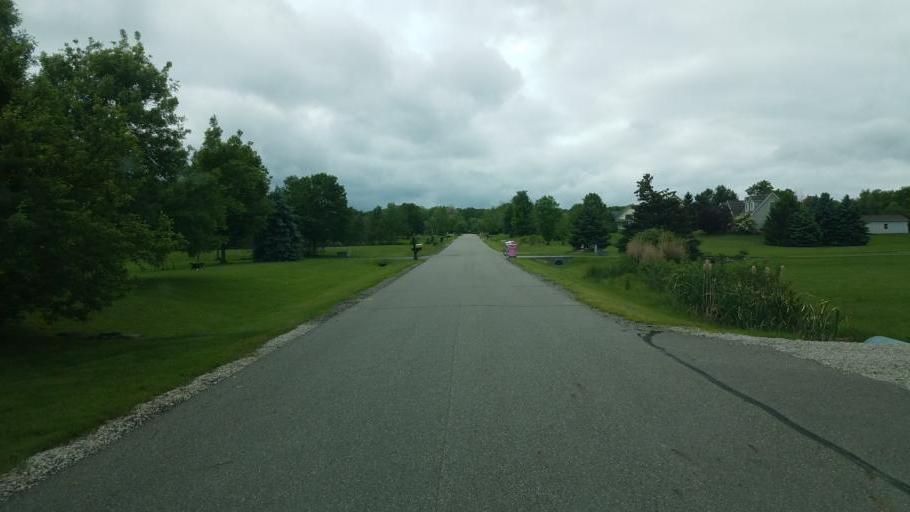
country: US
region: Ohio
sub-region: Geauga County
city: Burton
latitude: 41.4238
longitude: -81.2044
